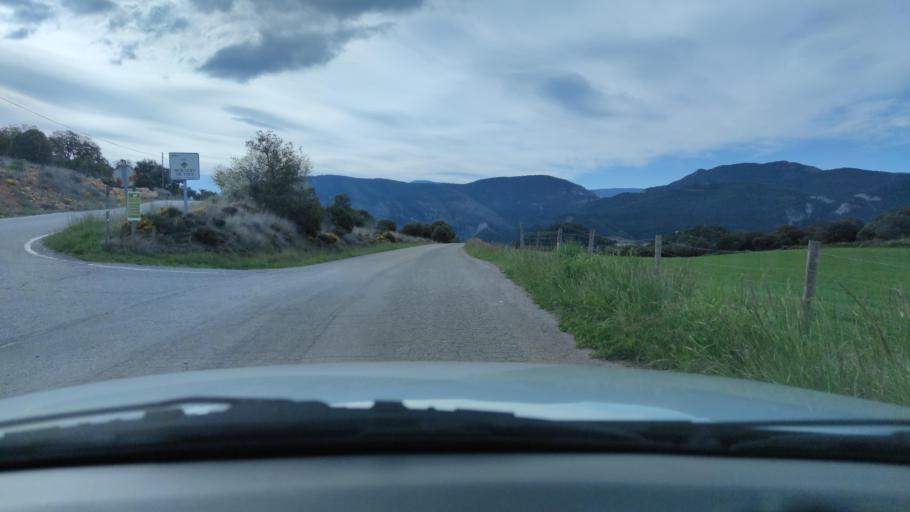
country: ES
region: Catalonia
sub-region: Provincia de Lleida
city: Coll de Nargo
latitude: 42.2386
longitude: 1.3804
